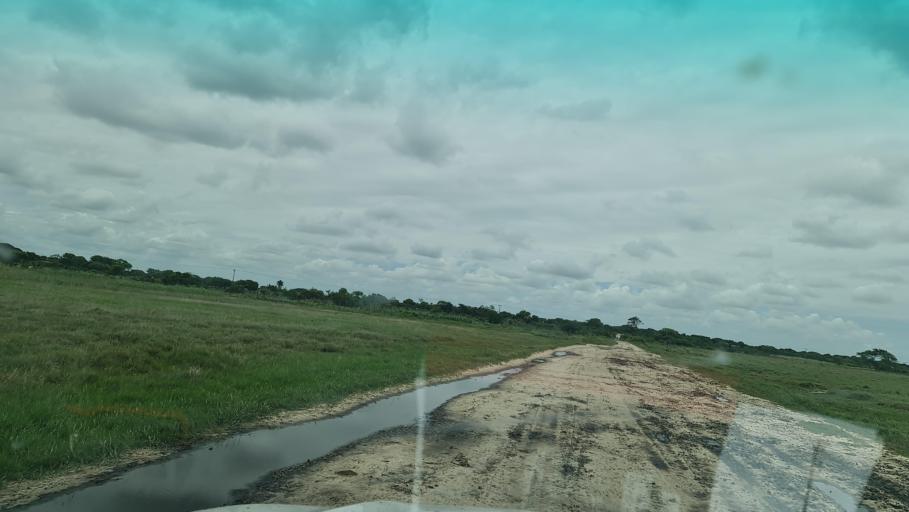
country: MZ
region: Maputo City
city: Maputo
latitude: -25.7038
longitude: 32.7040
